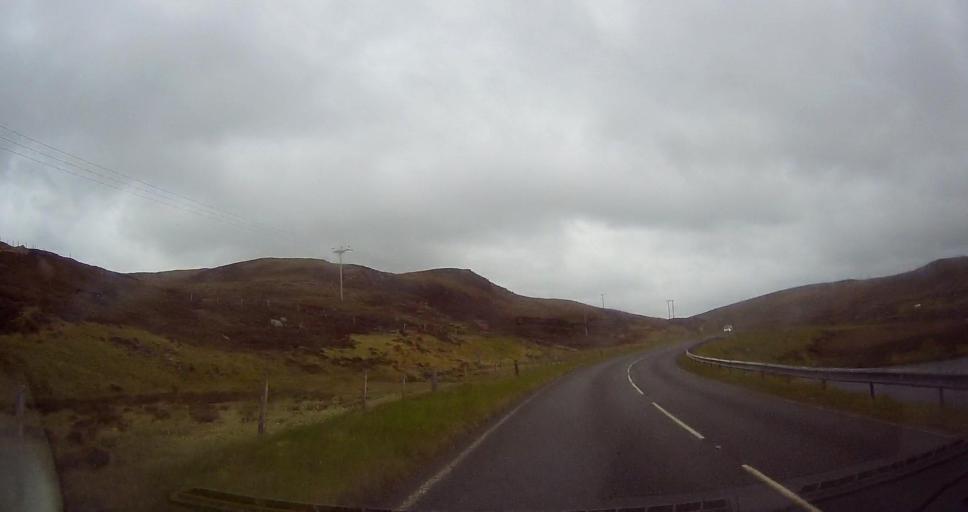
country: GB
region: Scotland
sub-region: Shetland Islands
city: Lerwick
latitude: 60.4430
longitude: -1.3957
